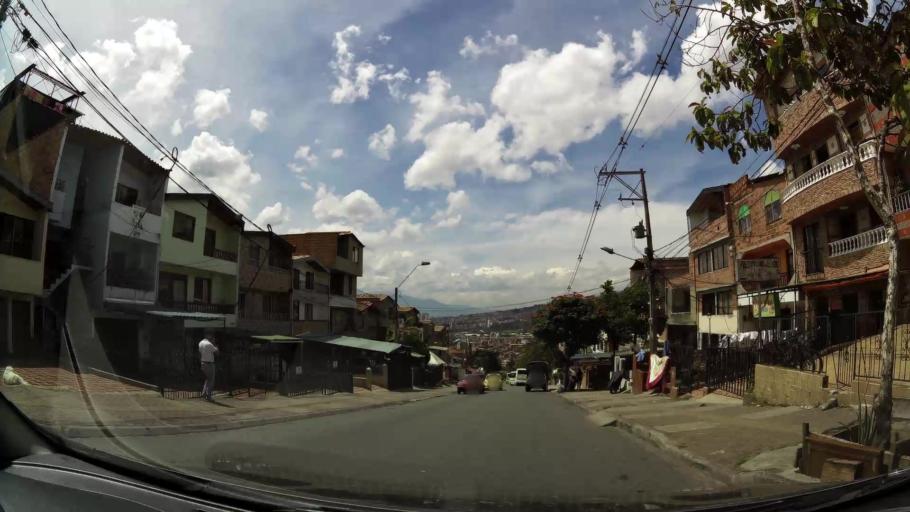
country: CO
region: Antioquia
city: Bello
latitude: 6.3473
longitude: -75.5545
